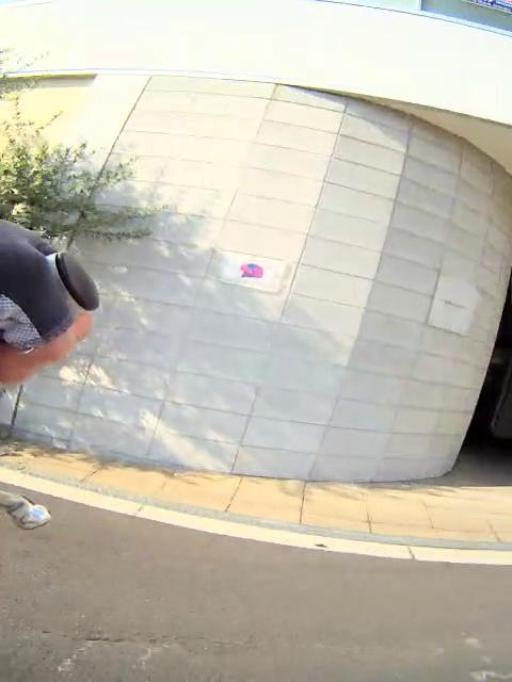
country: JP
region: Osaka
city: Suita
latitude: 34.7387
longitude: 135.5177
